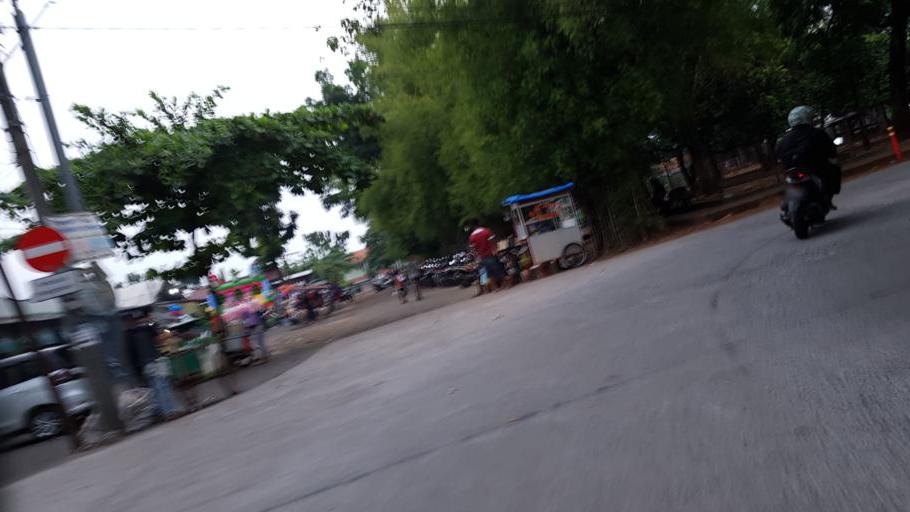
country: ID
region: West Java
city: Depok
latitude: -6.3405
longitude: 106.8443
